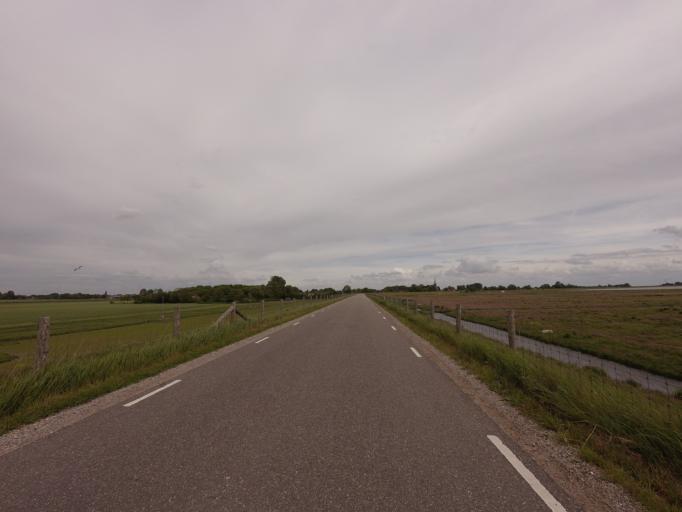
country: NL
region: North Holland
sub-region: Gemeente Hoorn
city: Hoorn
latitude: 52.6358
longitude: 5.1115
